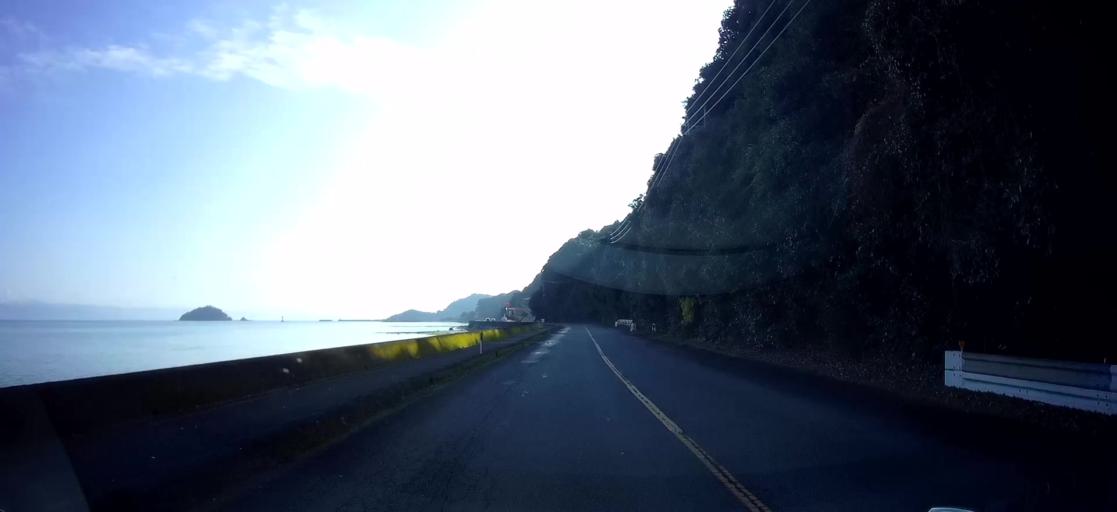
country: JP
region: Kumamoto
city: Yatsushiro
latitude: 32.4842
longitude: 130.4371
